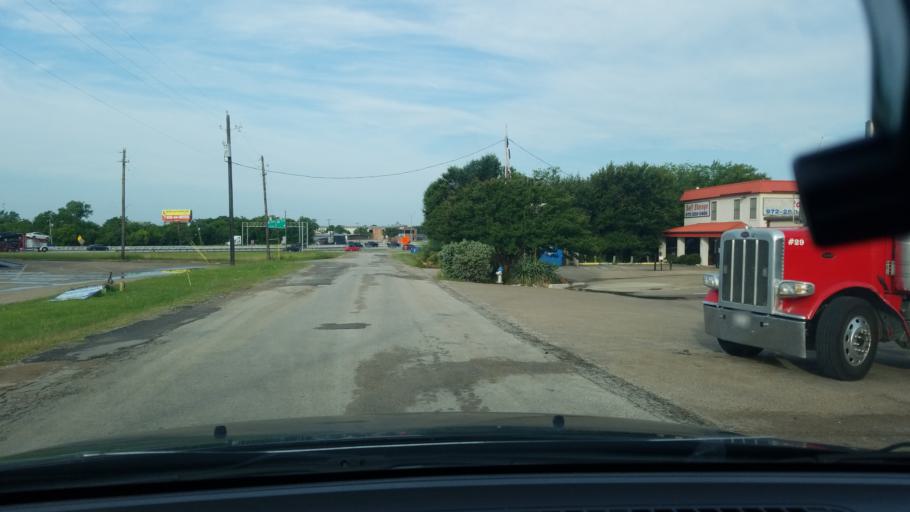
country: US
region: Texas
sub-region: Dallas County
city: Mesquite
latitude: 32.7942
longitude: -96.6175
